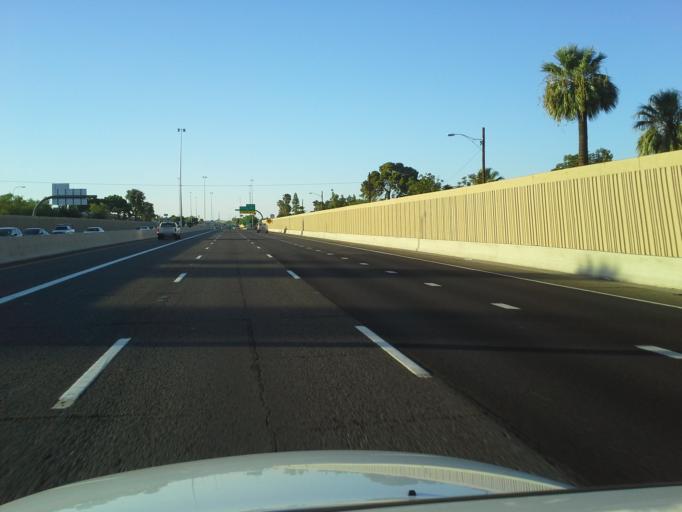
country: US
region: Arizona
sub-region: Maricopa County
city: Glendale
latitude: 33.5181
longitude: -112.1122
